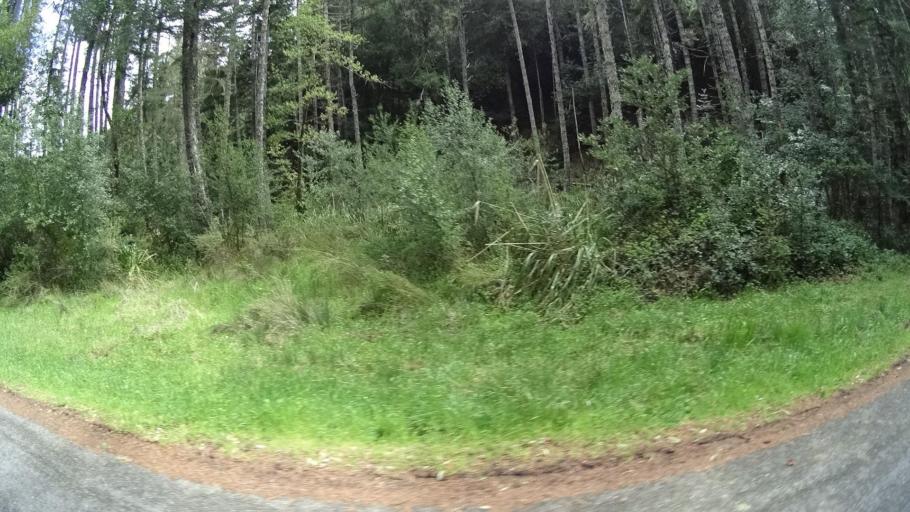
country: US
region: California
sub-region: Humboldt County
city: Blue Lake
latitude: 40.7951
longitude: -123.9793
